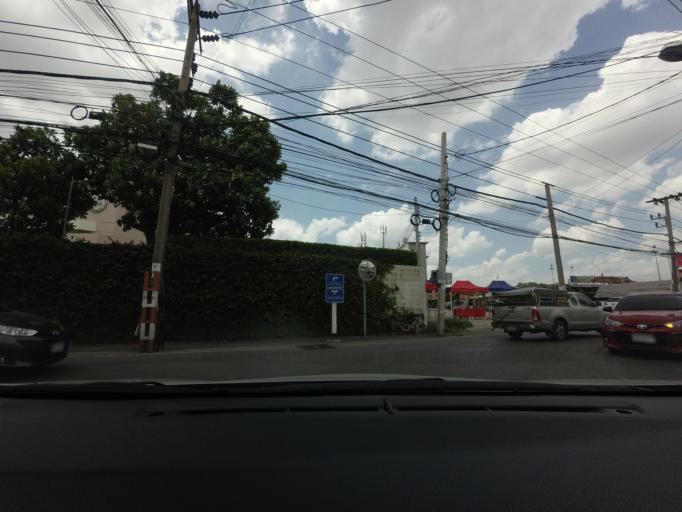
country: TH
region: Samut Prakan
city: Phra Samut Chedi
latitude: 13.6399
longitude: 100.5686
